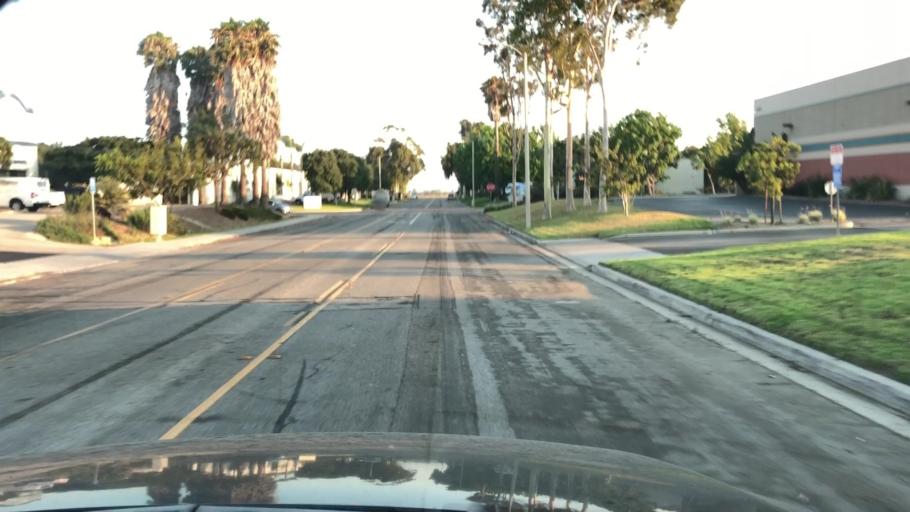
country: US
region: California
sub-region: Ventura County
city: Ventura
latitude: 34.2553
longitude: -119.2325
